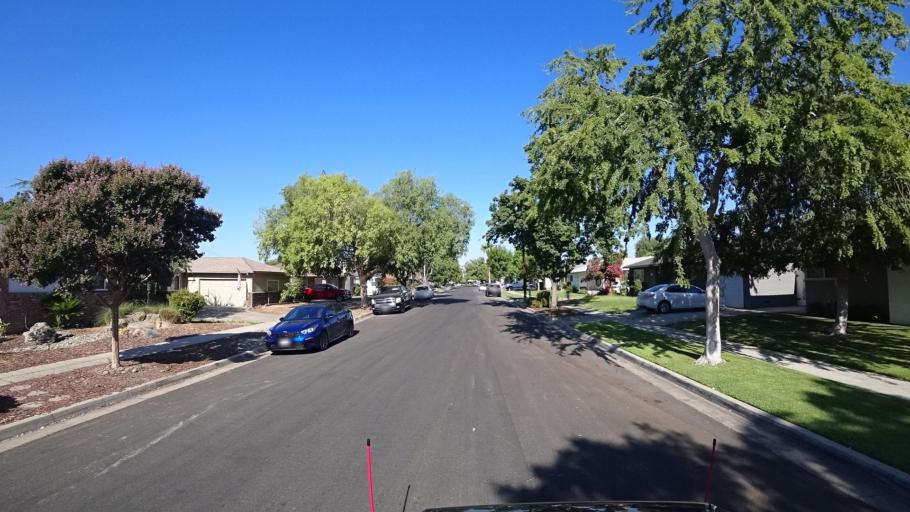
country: US
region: California
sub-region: Fresno County
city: Fresno
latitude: 36.7846
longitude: -119.7645
